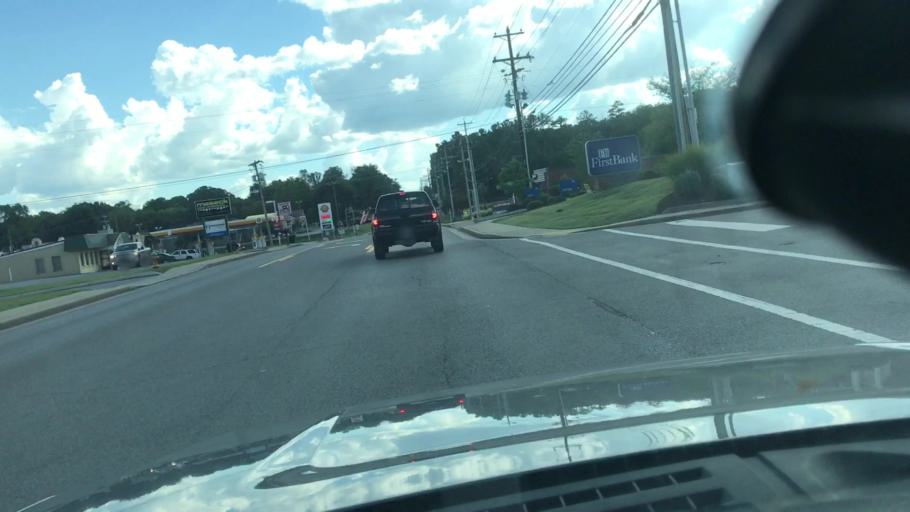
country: US
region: Tennessee
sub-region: Williamson County
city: Fairview
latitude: 35.9746
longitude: -87.1277
